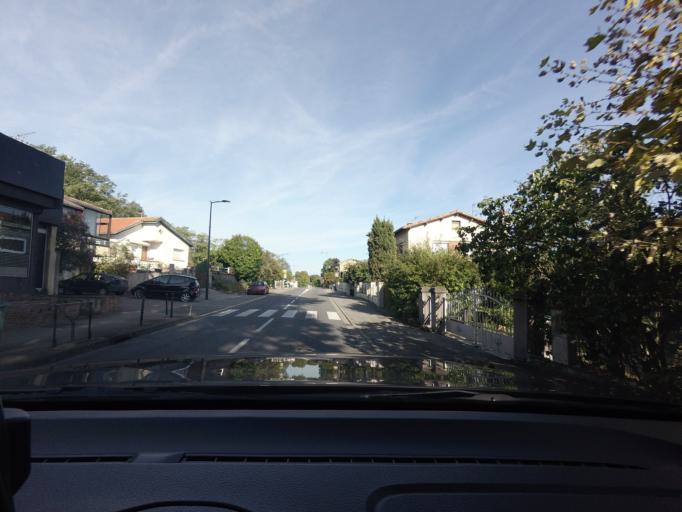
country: FR
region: Midi-Pyrenees
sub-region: Departement de la Haute-Garonne
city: Cornebarrieu
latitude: 43.6511
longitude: 1.3324
